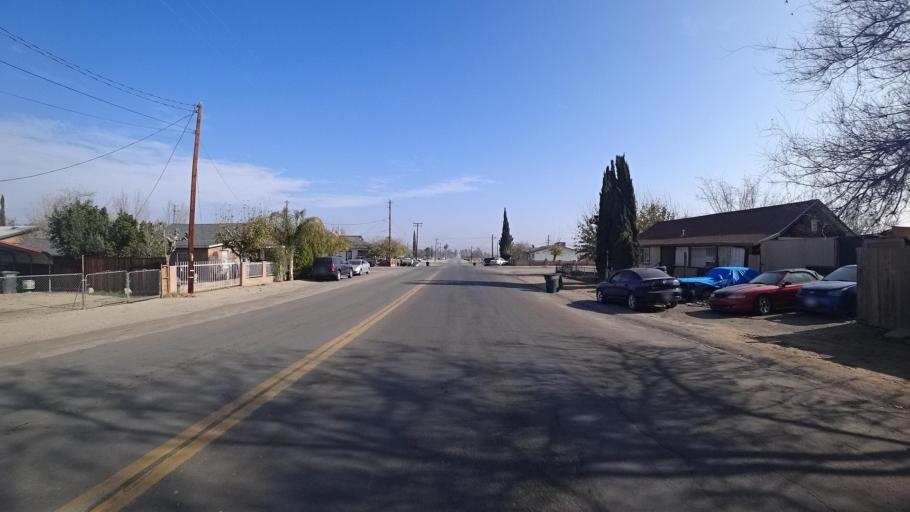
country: US
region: California
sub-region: Kern County
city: Ford City
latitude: 35.1546
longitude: -119.4492
